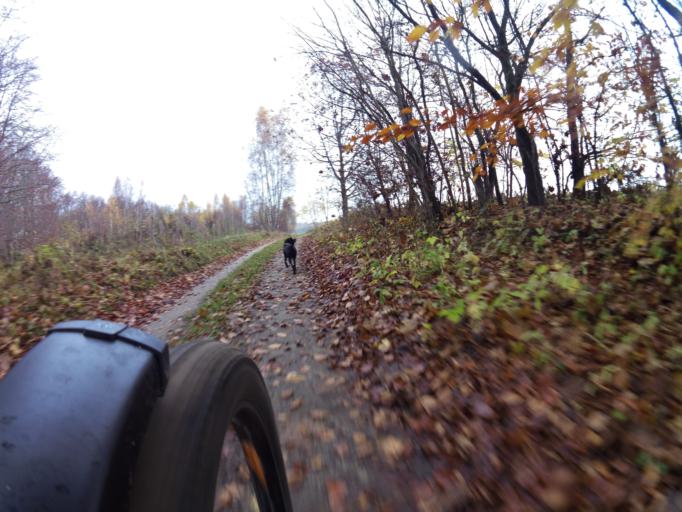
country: PL
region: Pomeranian Voivodeship
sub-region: Powiat pucki
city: Krokowa
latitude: 54.7235
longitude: 18.1326
